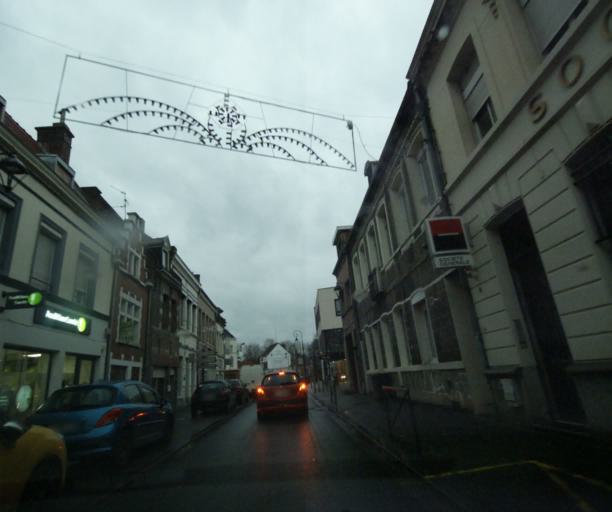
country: FR
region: Nord-Pas-de-Calais
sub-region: Departement du Nord
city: Conde-sur-l'Escaut
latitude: 50.4504
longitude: 3.5940
